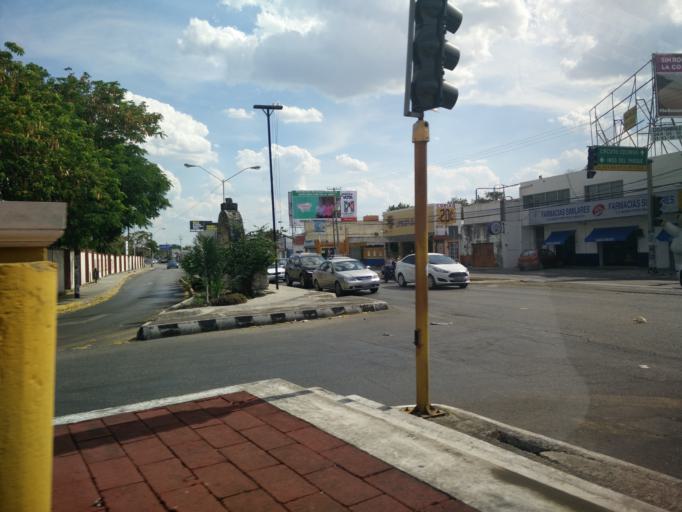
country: MX
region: Yucatan
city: Merida
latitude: 20.9694
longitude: -89.5910
